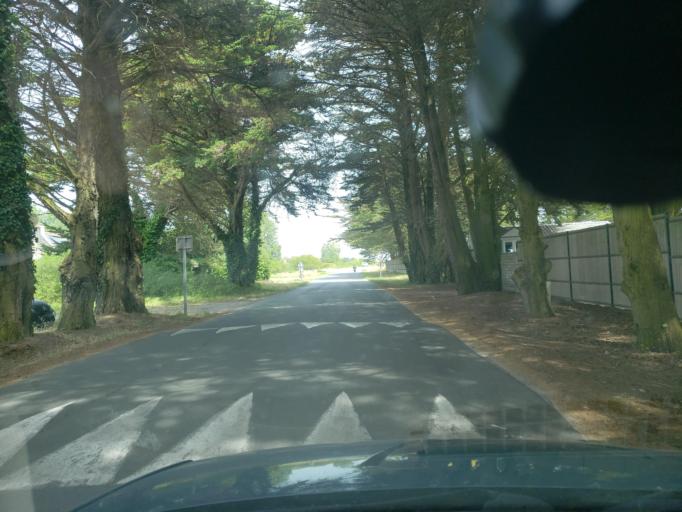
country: FR
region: Brittany
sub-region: Departement du Finistere
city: Guilvinec
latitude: 47.8040
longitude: -4.3120
